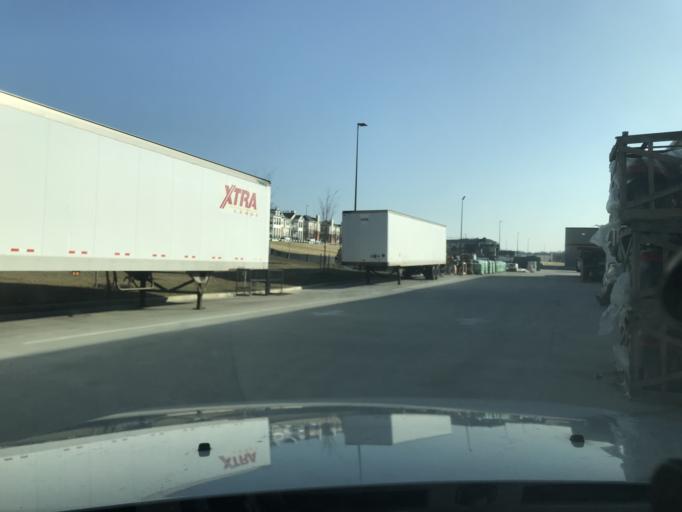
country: US
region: Maryland
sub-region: Baltimore County
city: Owings Mills
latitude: 39.4084
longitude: -76.7915
